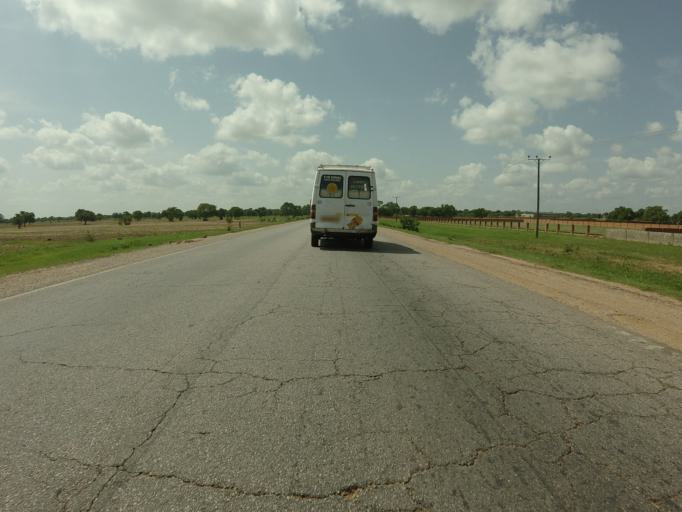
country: GH
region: Northern
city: Savelugu
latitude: 9.5667
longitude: -0.8356
